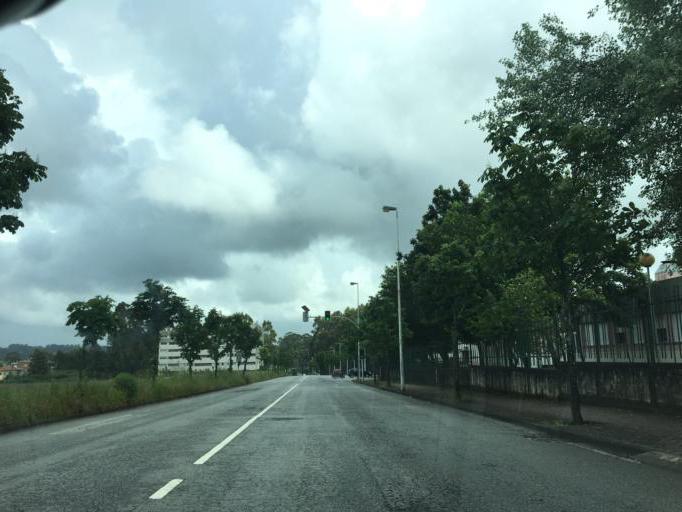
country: PT
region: Porto
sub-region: Maia
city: Anta
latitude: 41.2599
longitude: -8.6135
